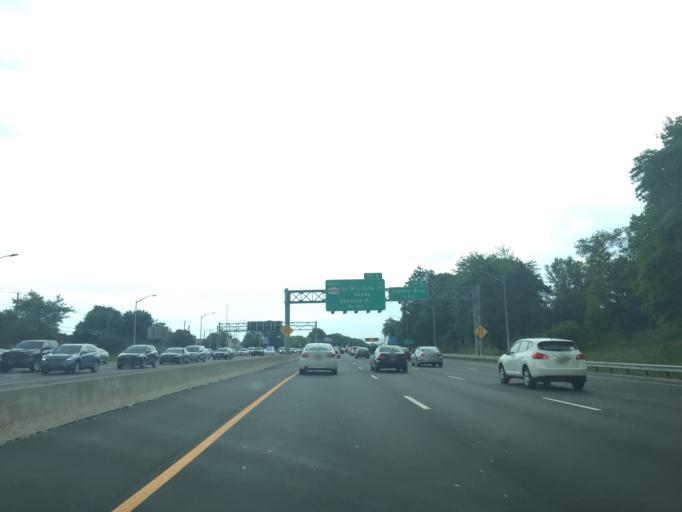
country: US
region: New York
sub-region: Richmond County
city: Bloomfield
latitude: 40.6187
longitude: -74.1632
